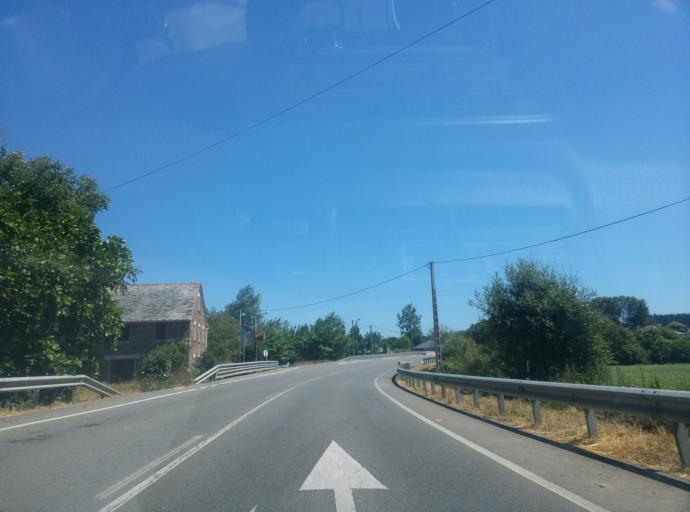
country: ES
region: Galicia
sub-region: Provincia de Lugo
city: Castro de Rei
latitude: 43.2480
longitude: -7.4148
